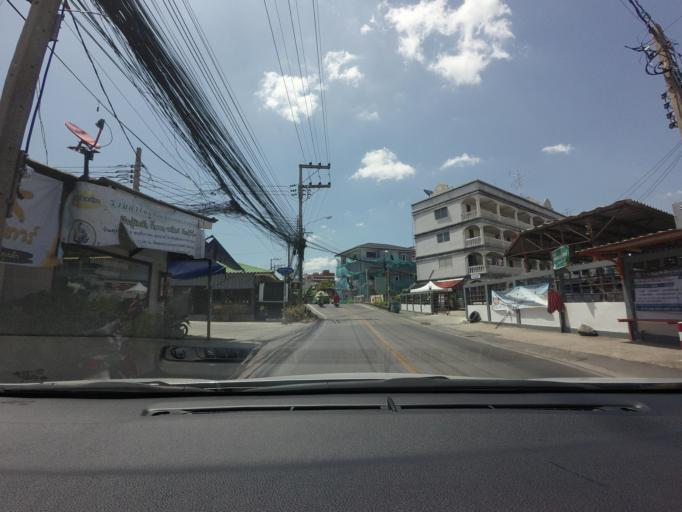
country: TH
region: Bangkok
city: Phra Khanong
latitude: 13.7272
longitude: 100.6133
